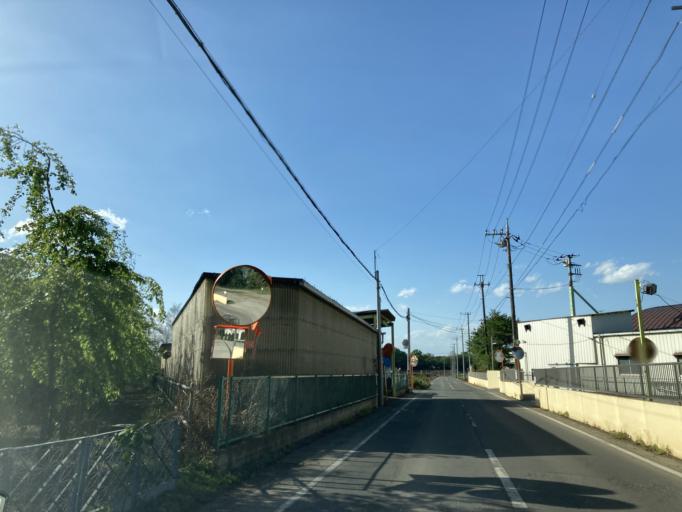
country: JP
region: Saitama
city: Sayama
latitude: 35.8561
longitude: 139.4428
